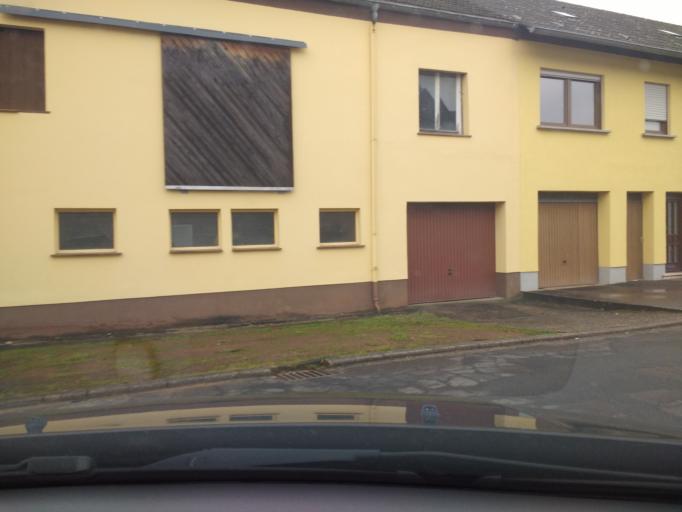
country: DE
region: Rheinland-Pfalz
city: Zerf
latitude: 49.5916
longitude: 6.6759
